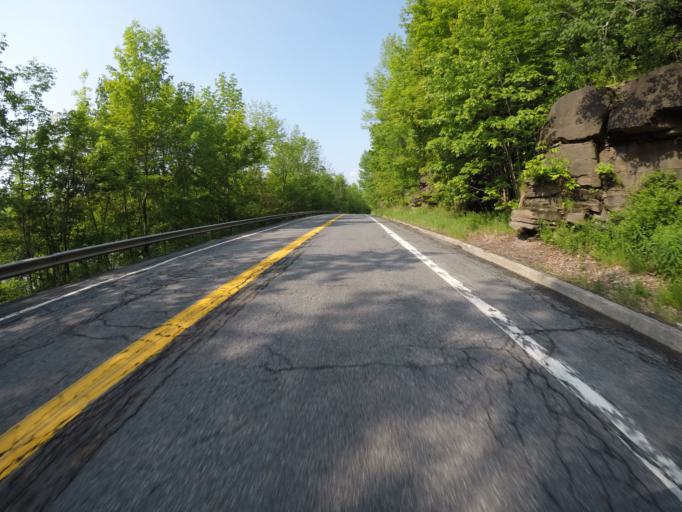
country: US
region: New York
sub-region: Sullivan County
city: Livingston Manor
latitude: 42.1062
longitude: -74.7819
